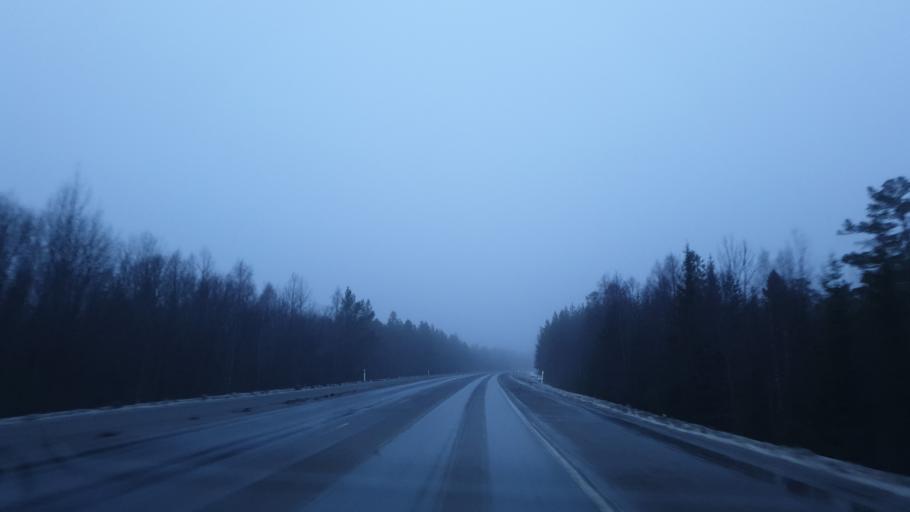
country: SE
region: Vaesterbotten
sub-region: Umea Kommun
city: Holmsund
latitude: 63.7578
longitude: 20.3504
